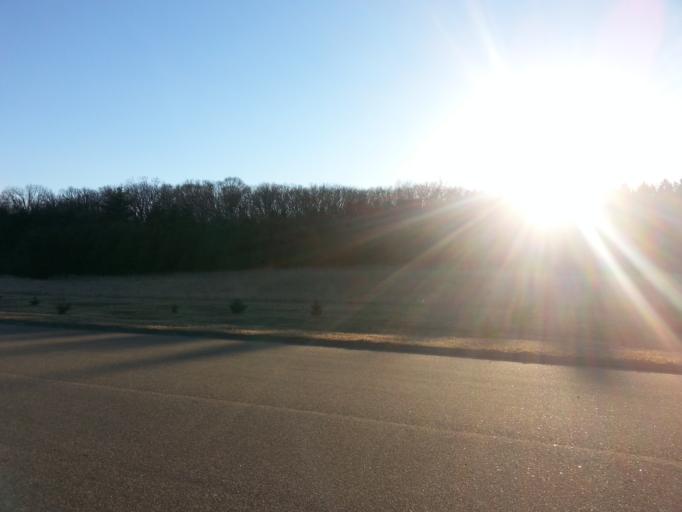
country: US
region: Minnesota
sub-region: Washington County
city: Lake Elmo
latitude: 44.9801
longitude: -92.8365
